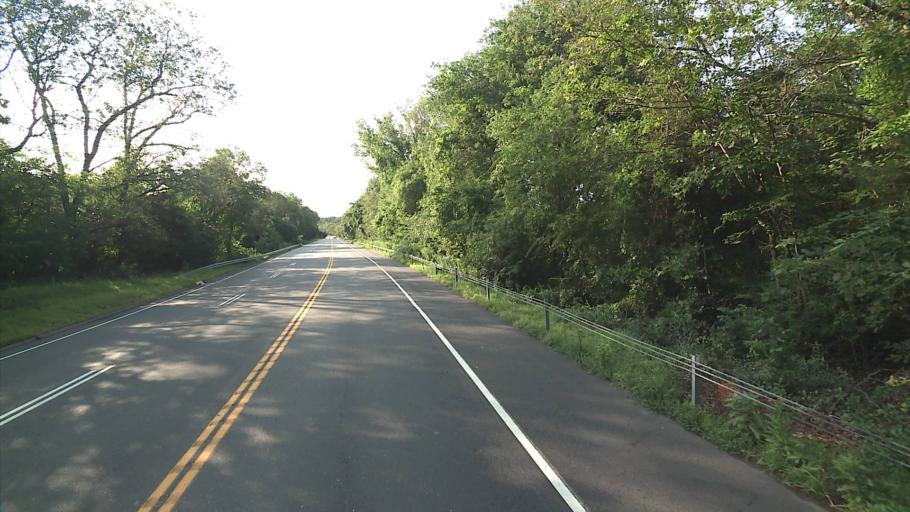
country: US
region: Connecticut
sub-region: New London County
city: Norwich
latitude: 41.5071
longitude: -72.0441
